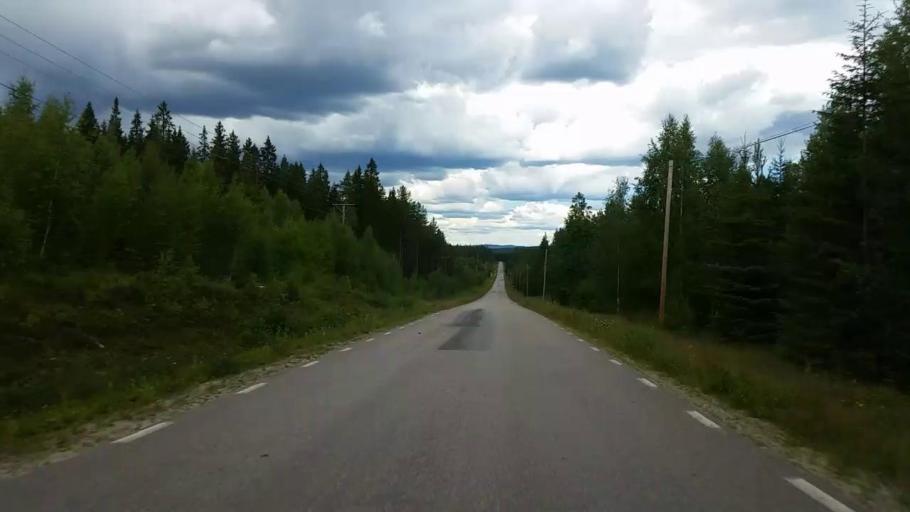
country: SE
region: Gaevleborg
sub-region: Ovanakers Kommun
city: Edsbyn
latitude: 61.4185
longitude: 15.9002
